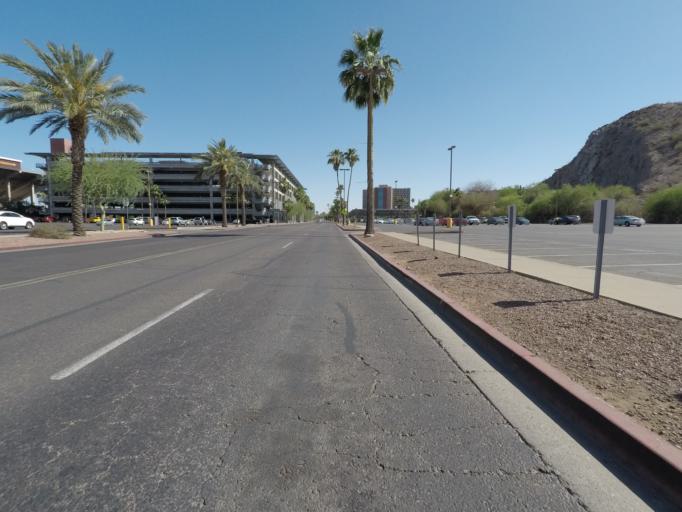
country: US
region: Arizona
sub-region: Maricopa County
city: Tempe Junction
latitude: 33.4271
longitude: -111.9292
